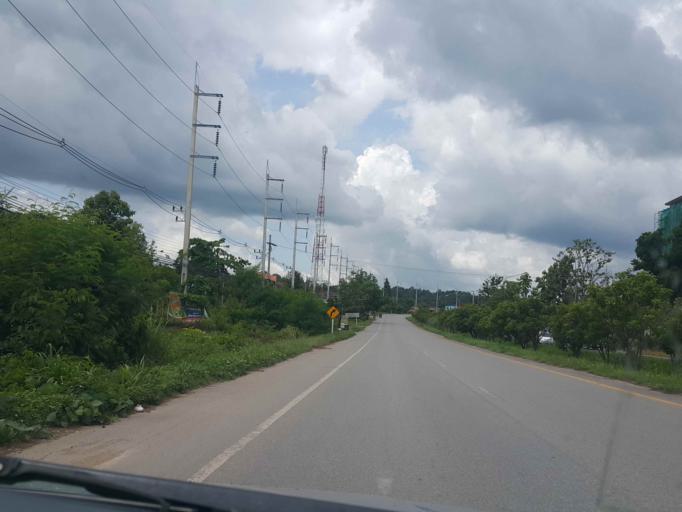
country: TH
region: Phayao
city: Dok Kham Tai
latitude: 19.0234
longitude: 99.9216
